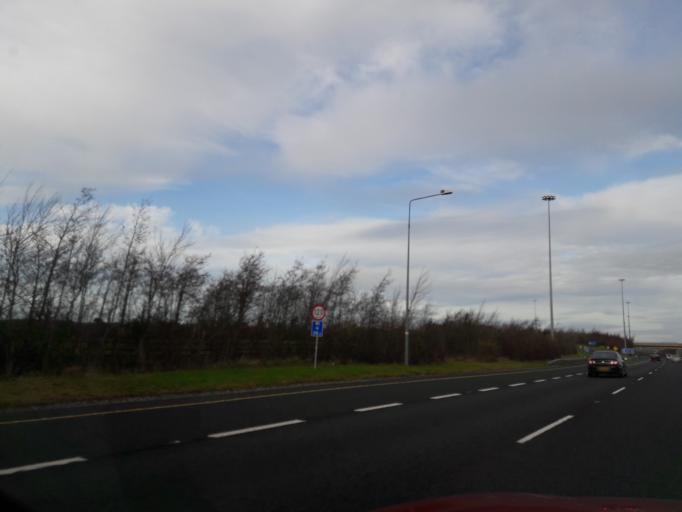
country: IE
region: Leinster
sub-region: Lu
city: Drogheda
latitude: 53.6994
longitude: -6.3795
